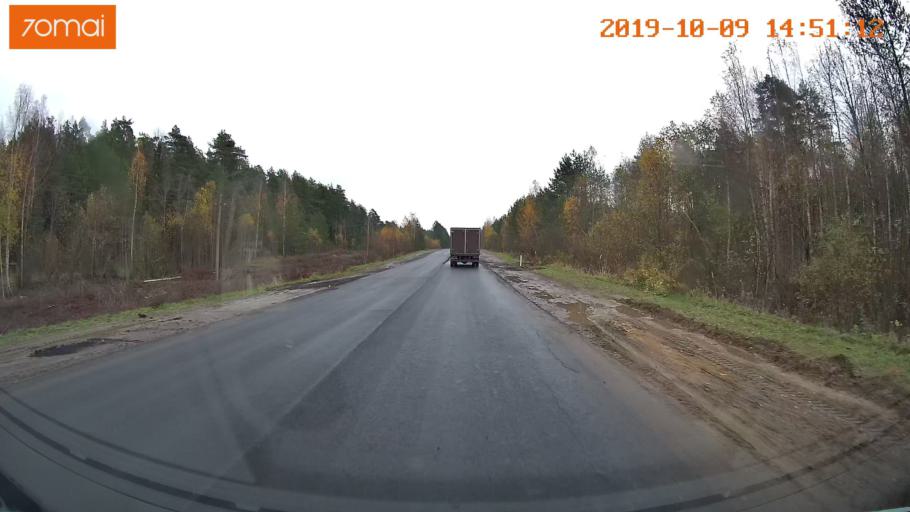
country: RU
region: Kostroma
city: Chistyye Bory
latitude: 58.3791
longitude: 41.6117
